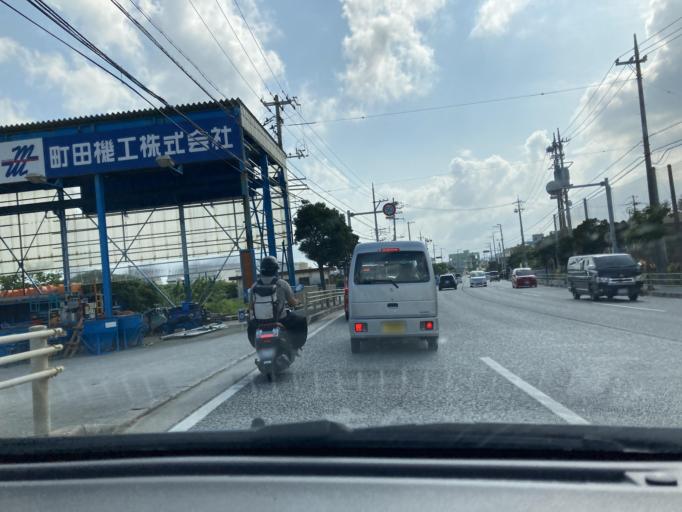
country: JP
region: Okinawa
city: Chatan
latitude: 26.2816
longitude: 127.8150
